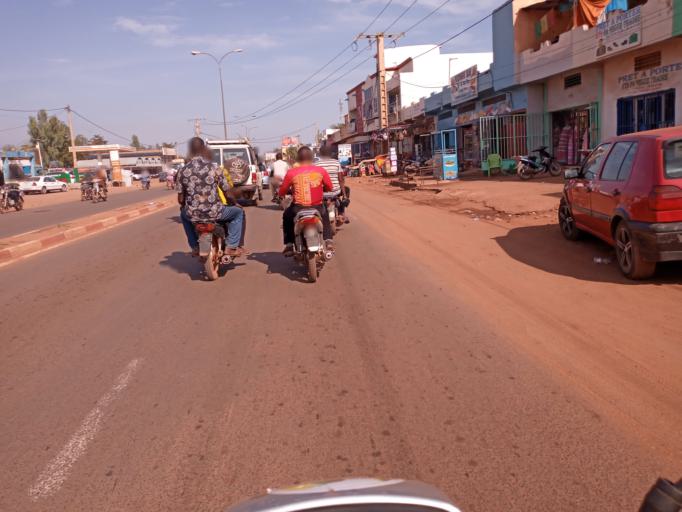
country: ML
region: Bamako
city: Bamako
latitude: 12.6657
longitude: -7.9339
